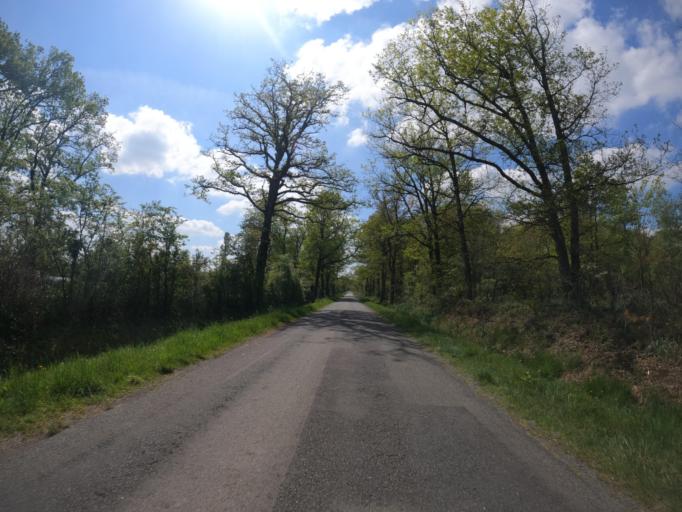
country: FR
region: Poitou-Charentes
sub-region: Departement des Deux-Sevres
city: Chiche
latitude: 46.7921
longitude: -0.3009
